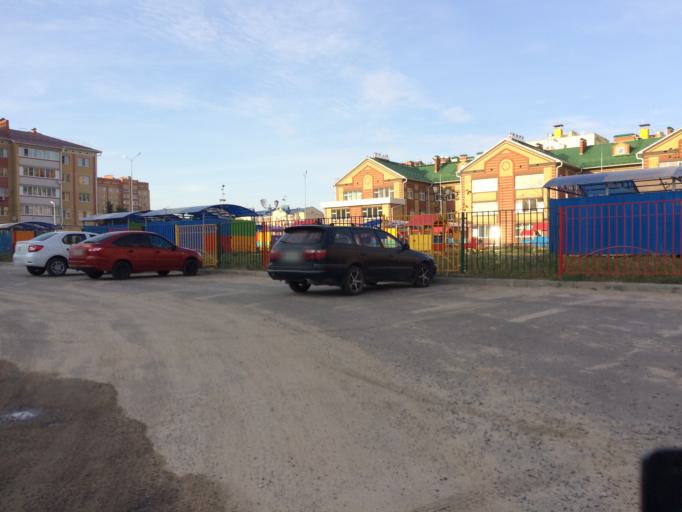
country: RU
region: Mariy-El
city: Yoshkar-Ola
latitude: 56.6273
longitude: 47.8499
